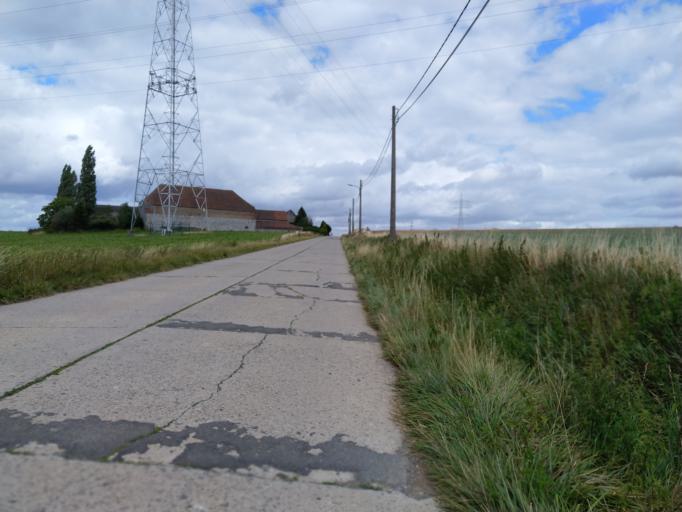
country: BE
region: Wallonia
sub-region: Province du Hainaut
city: Anderlues
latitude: 50.3889
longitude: 4.3450
